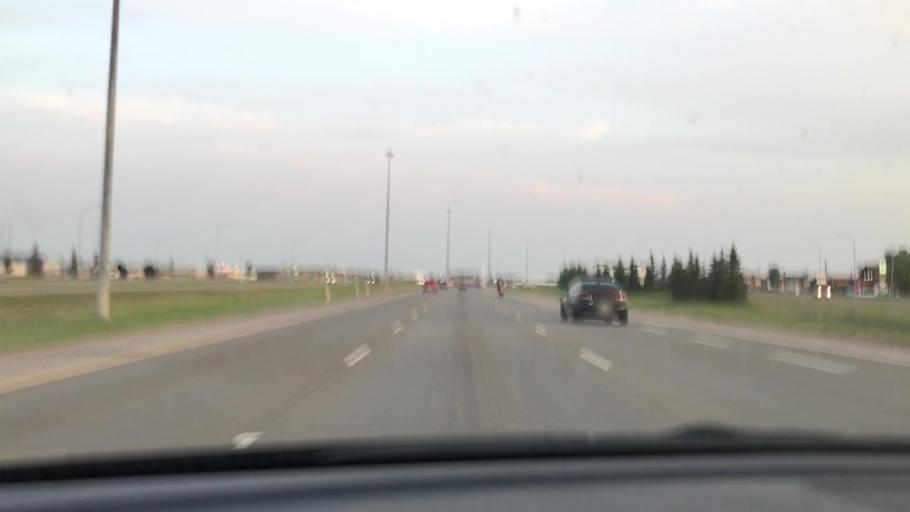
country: CA
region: Alberta
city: Airdrie
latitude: 51.2965
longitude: -114.0014
